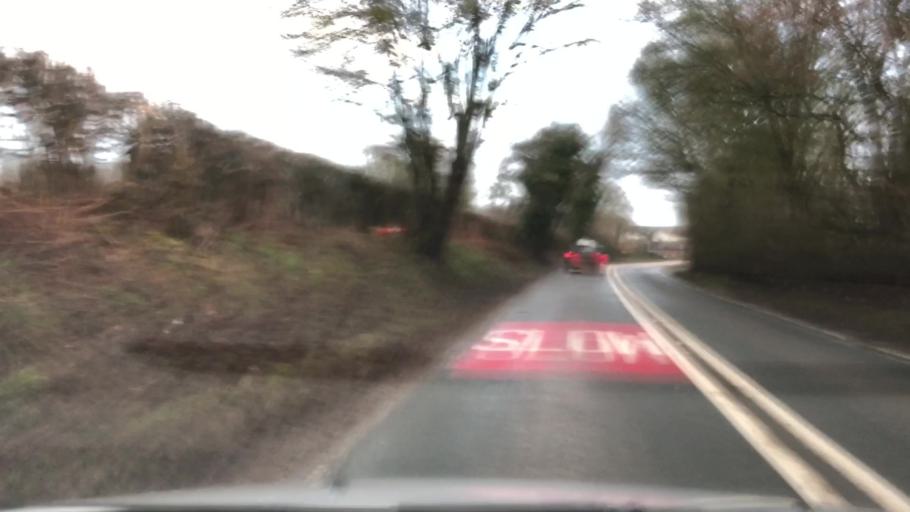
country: GB
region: England
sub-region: Hampshire
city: Alton
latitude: 51.1858
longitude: -0.9880
